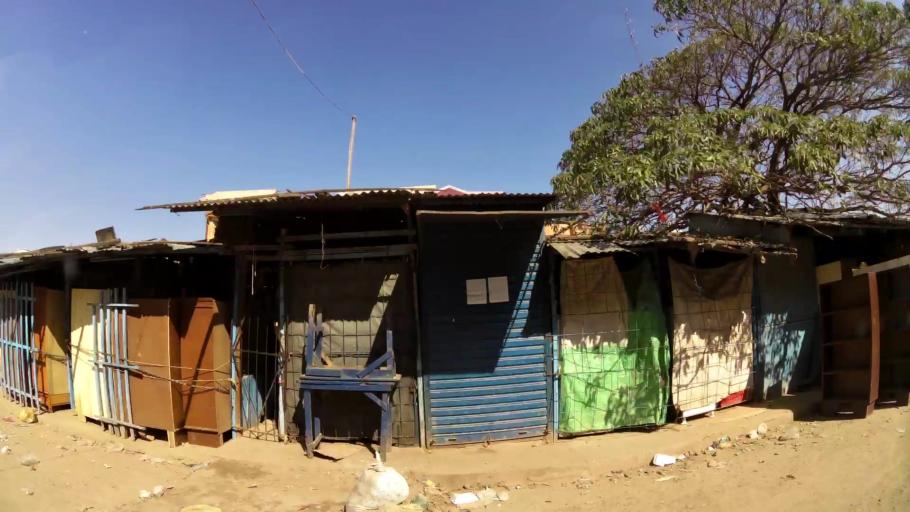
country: BO
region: Santa Cruz
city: Santa Cruz de la Sierra
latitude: -17.8256
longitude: -63.1328
